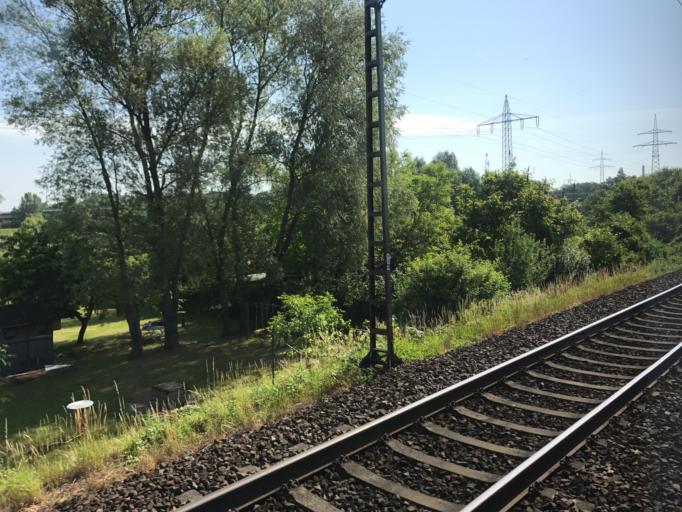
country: DE
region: Rheinland-Pfalz
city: Budenheim
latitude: 50.0270
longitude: 8.2064
